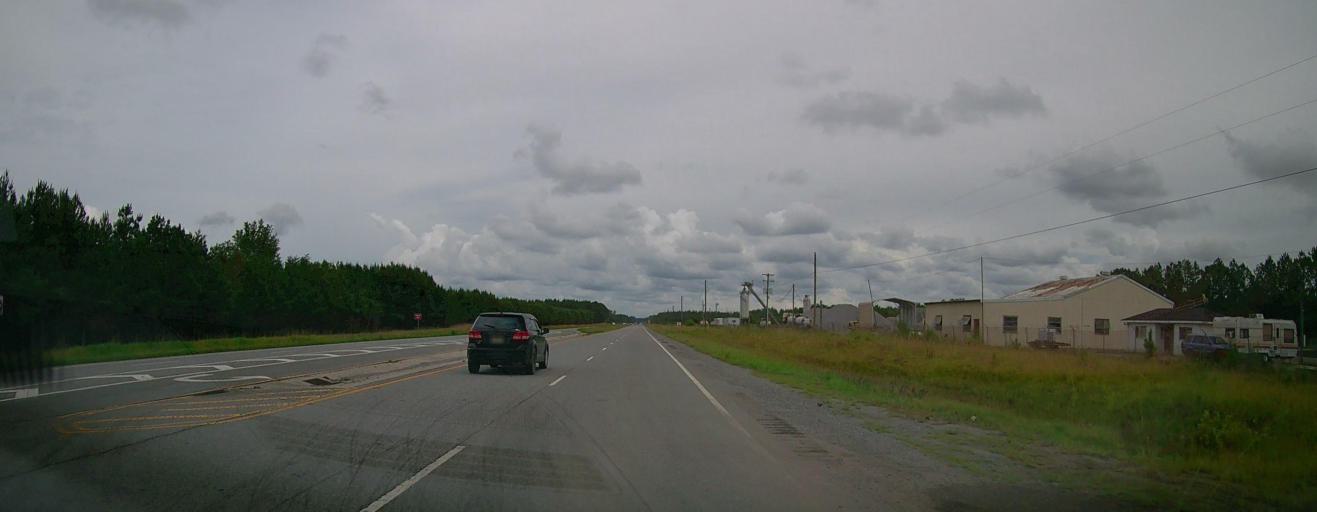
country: US
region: Georgia
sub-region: Appling County
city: Baxley
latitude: 31.7377
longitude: -82.2318
